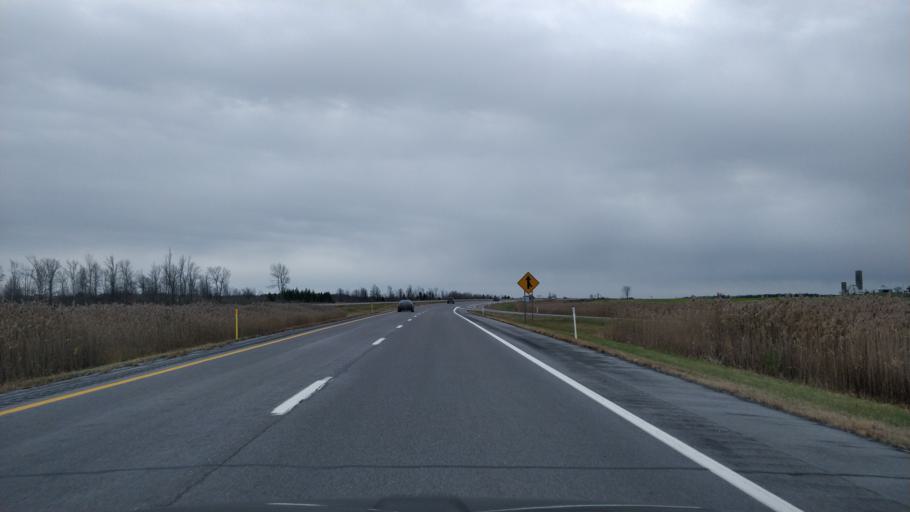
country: US
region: New York
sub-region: Jefferson County
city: Calcium
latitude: 44.1621
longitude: -75.8789
